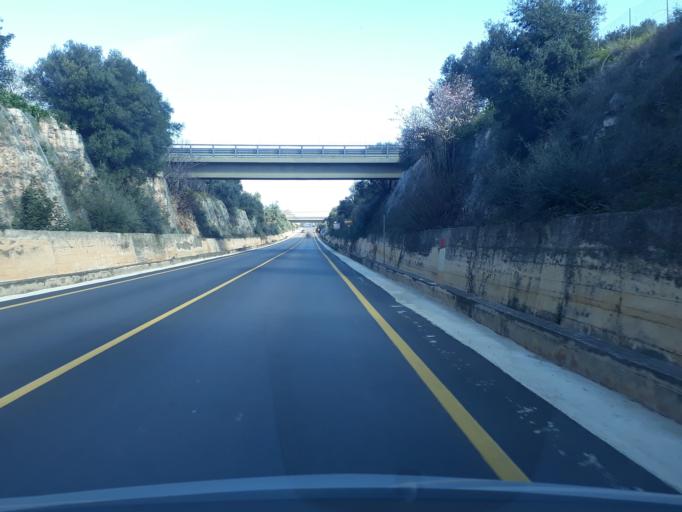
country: IT
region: Apulia
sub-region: Provincia di Brindisi
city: Fasano
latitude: 40.8384
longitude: 17.3512
